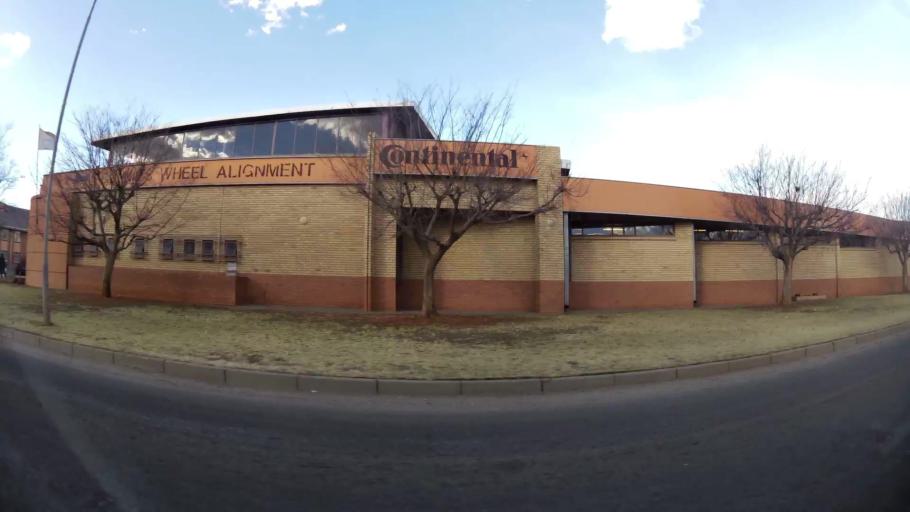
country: ZA
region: North-West
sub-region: Dr Kenneth Kaunda District Municipality
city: Klerksdorp
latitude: -26.8735
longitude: 26.6674
